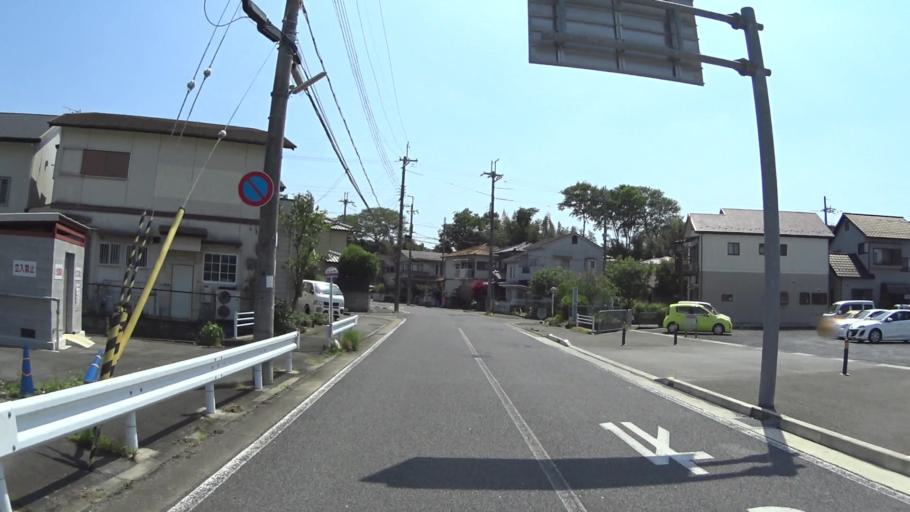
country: JP
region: Kyoto
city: Kameoka
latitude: 35.0242
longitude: 135.5661
